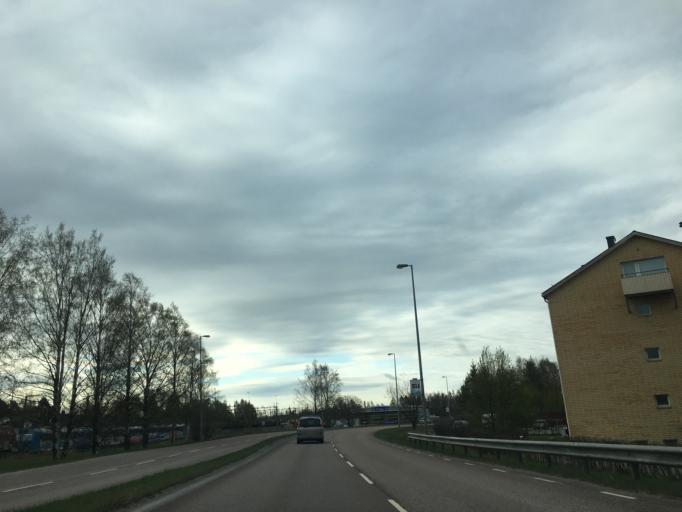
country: SE
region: Vaermland
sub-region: Kristinehamns Kommun
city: Kristinehamn
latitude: 59.3239
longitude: 14.0973
